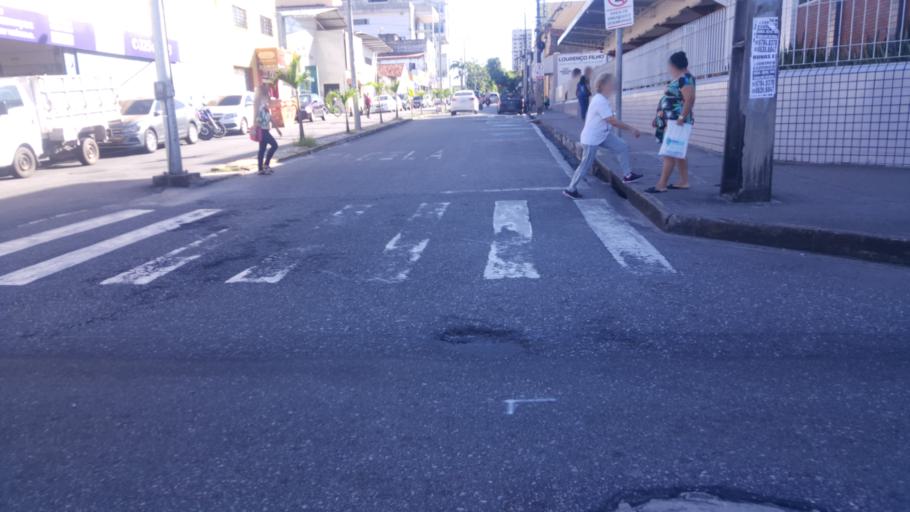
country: BR
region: Ceara
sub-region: Fortaleza
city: Fortaleza
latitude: -3.7366
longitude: -38.5315
